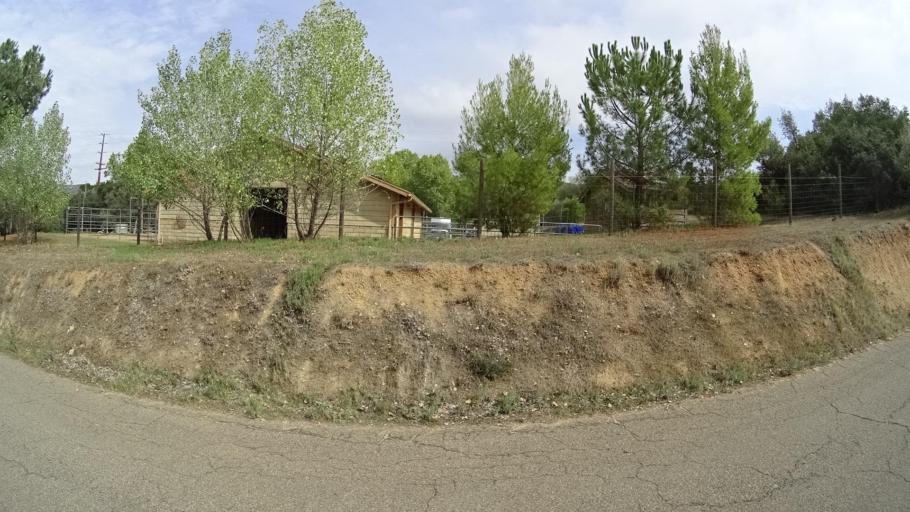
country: US
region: California
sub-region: San Diego County
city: Descanso
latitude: 32.8633
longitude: -116.6346
